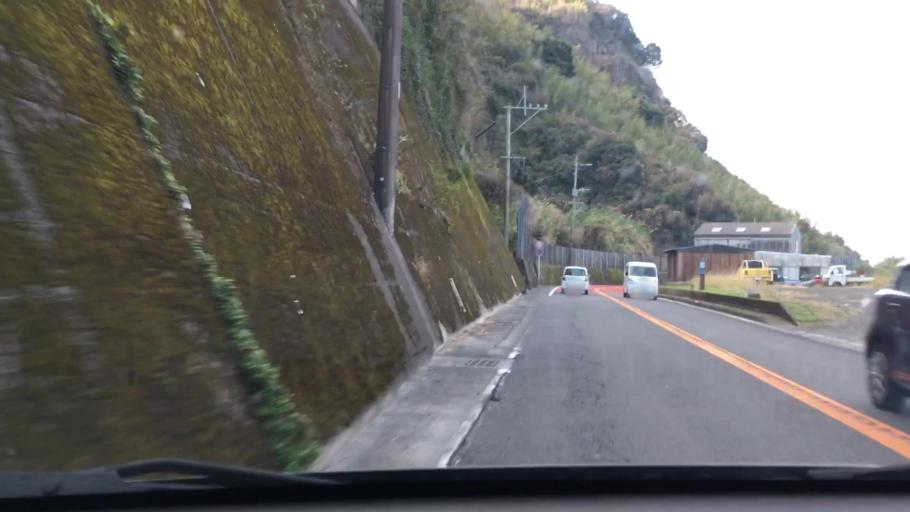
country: JP
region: Kagoshima
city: Hamanoichi
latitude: 31.6052
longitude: 130.7902
